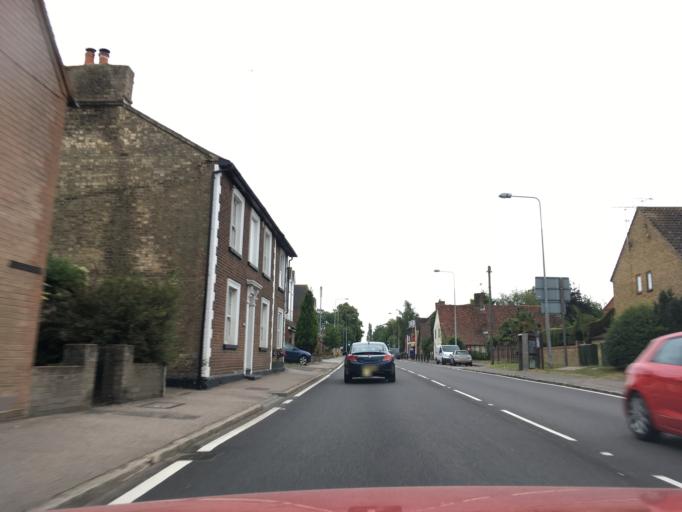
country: GB
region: England
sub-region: Central Bedfordshire
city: Hockliffe
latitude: 51.9299
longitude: -0.5850
